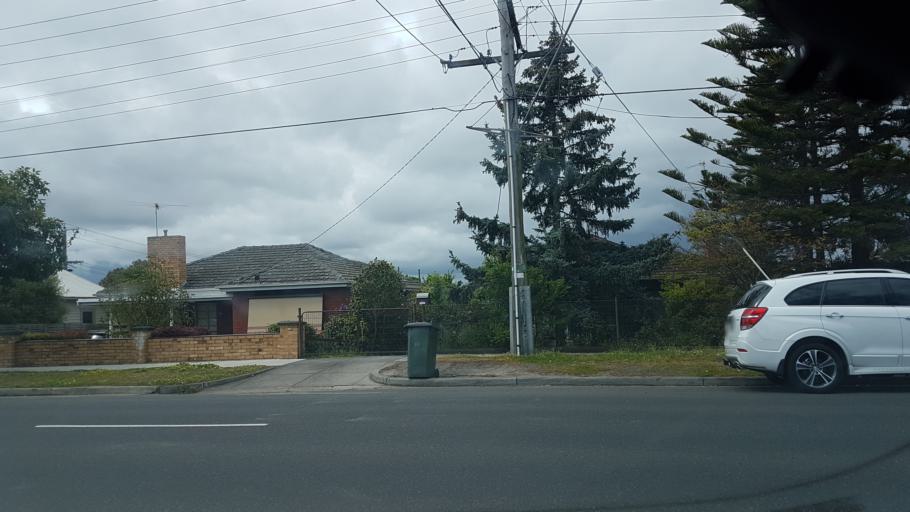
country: AU
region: Victoria
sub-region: Bayside
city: Moorabbin
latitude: -37.9318
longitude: 145.0393
